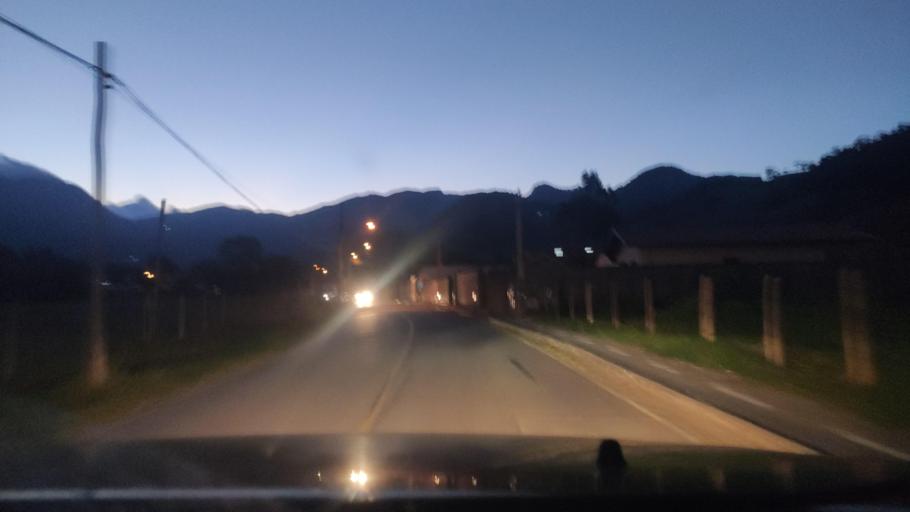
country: BR
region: Minas Gerais
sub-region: Paraisopolis
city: Paraisopolis
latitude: -22.7026
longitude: -45.7560
